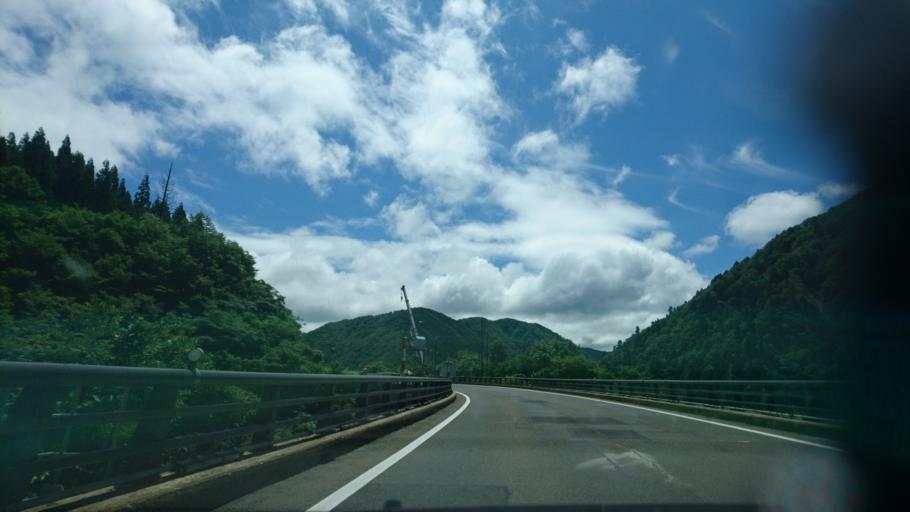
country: JP
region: Iwate
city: Shizukuishi
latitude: 39.6950
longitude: 140.7787
